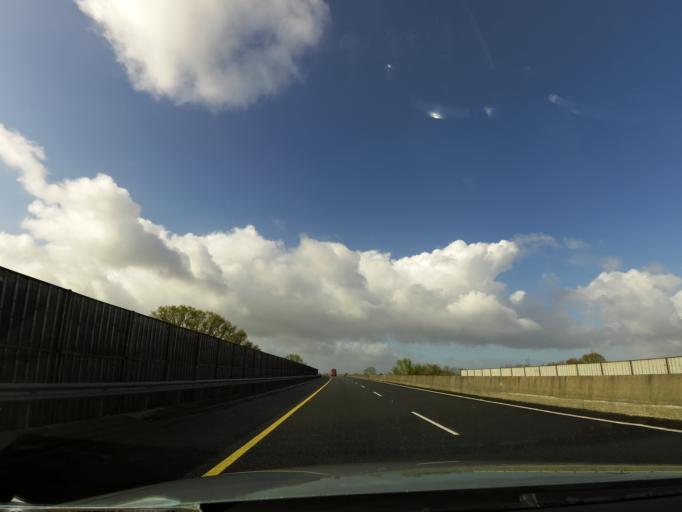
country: IE
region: Munster
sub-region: County Limerick
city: Castleconnell
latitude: 52.7101
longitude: -8.4796
